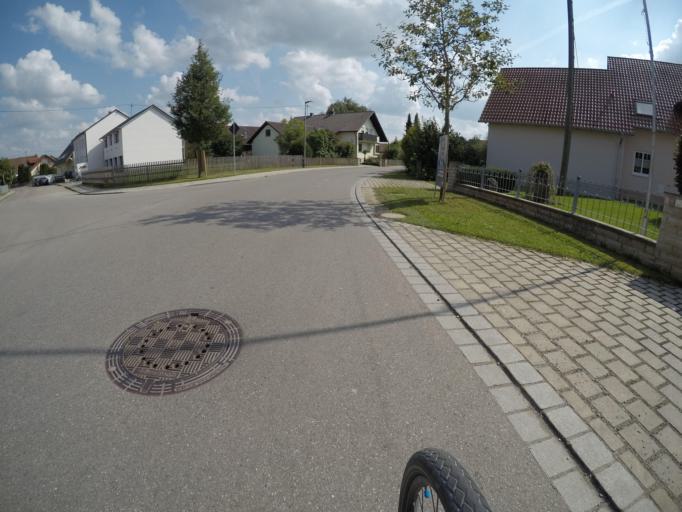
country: DE
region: Bavaria
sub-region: Swabia
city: Westendorf
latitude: 48.5703
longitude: 10.8374
